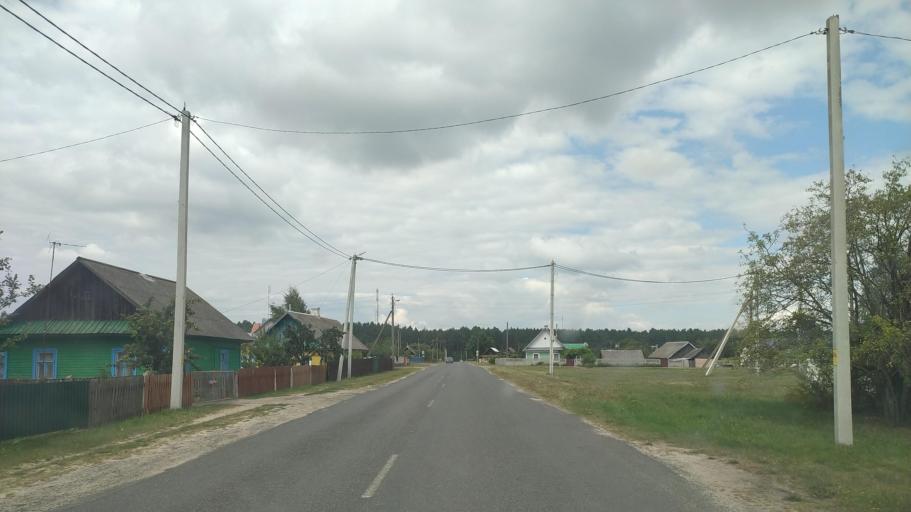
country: BY
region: Brest
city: Byaroza
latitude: 52.5438
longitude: 25.0679
